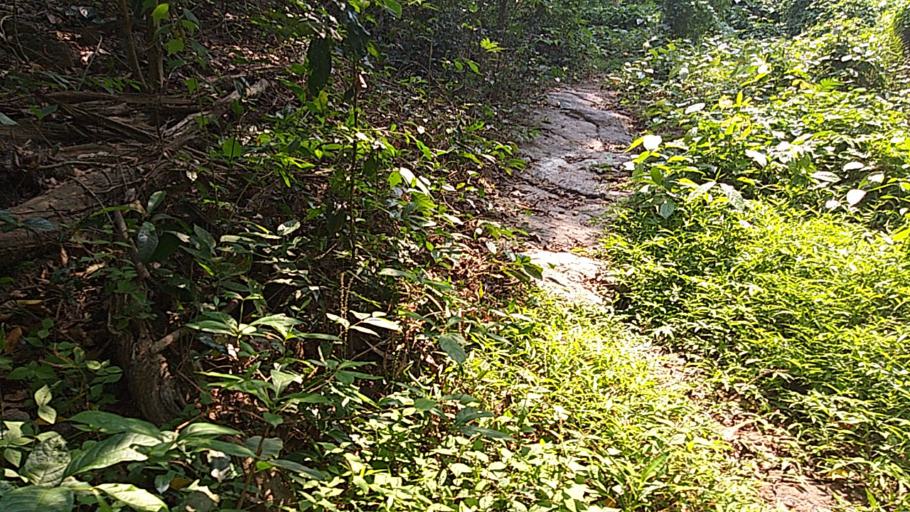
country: TH
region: Sara Buri
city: Wihan Daeng
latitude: 14.4342
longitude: 100.9614
